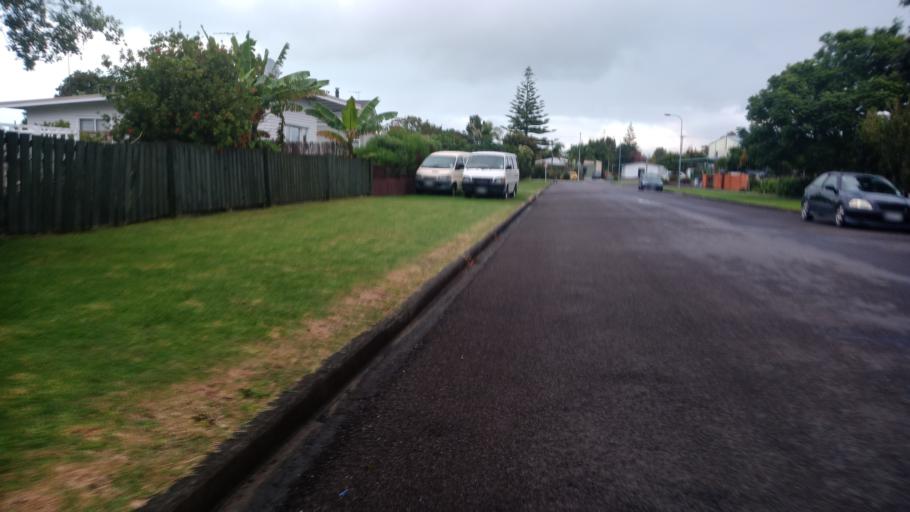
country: NZ
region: Gisborne
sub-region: Gisborne District
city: Gisborne
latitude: -38.6426
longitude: 178.0115
